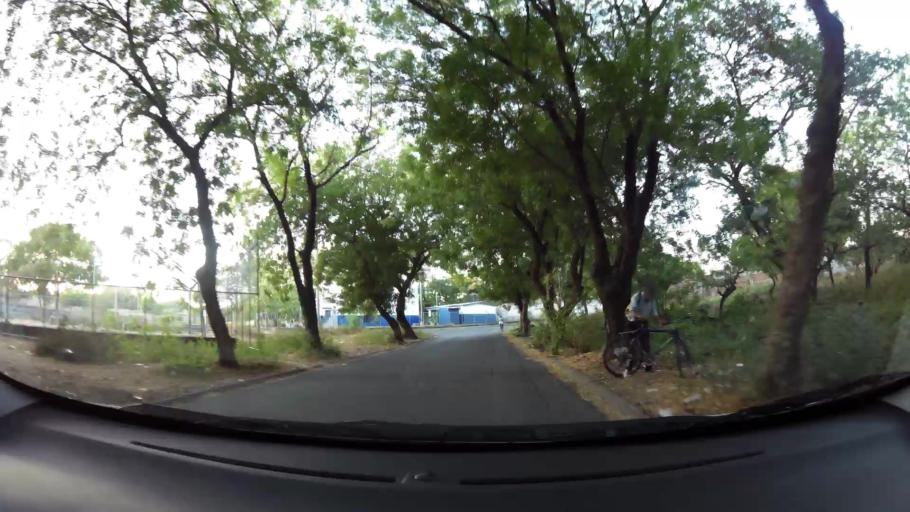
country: SV
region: San Miguel
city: San Miguel
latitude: 13.4832
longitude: -88.1595
